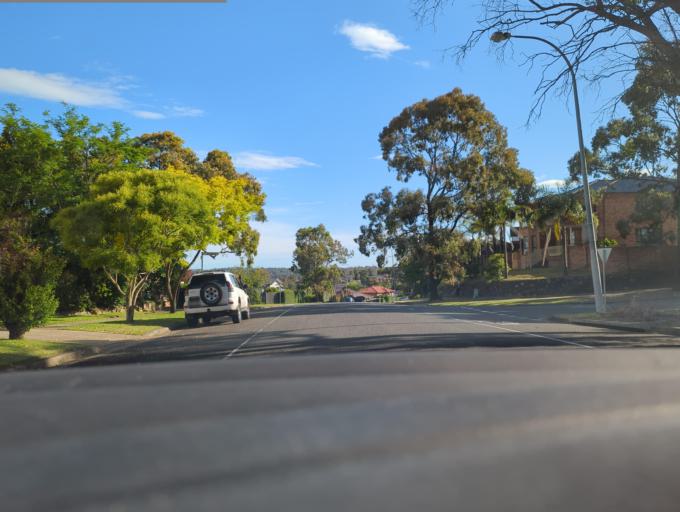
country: AU
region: New South Wales
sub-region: Sutherland Shire
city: Menai
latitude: -34.0264
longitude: 151.0132
